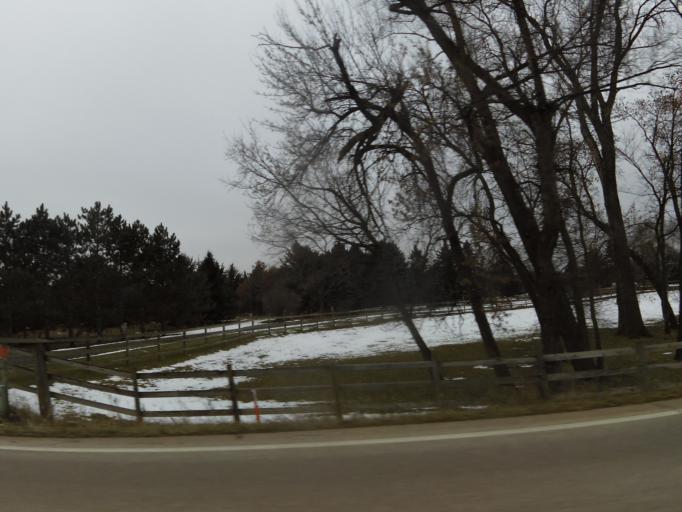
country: US
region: Minnesota
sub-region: Carver County
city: Carver
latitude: 44.7179
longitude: -93.6710
